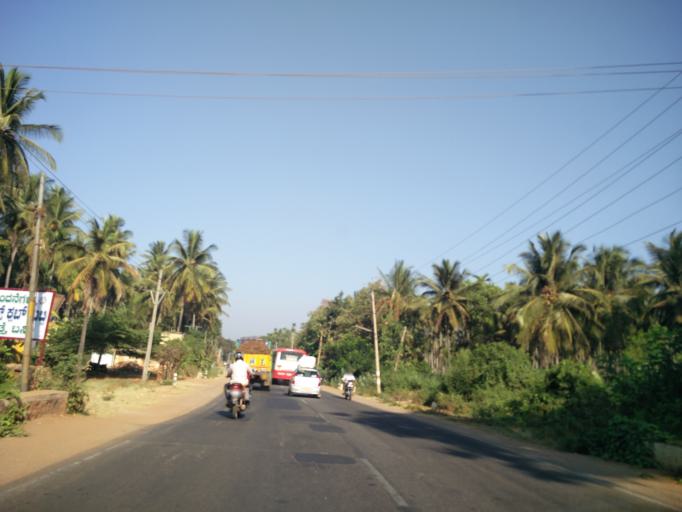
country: IN
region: Karnataka
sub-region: Tumkur
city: Gubbi
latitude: 13.3086
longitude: 76.9307
